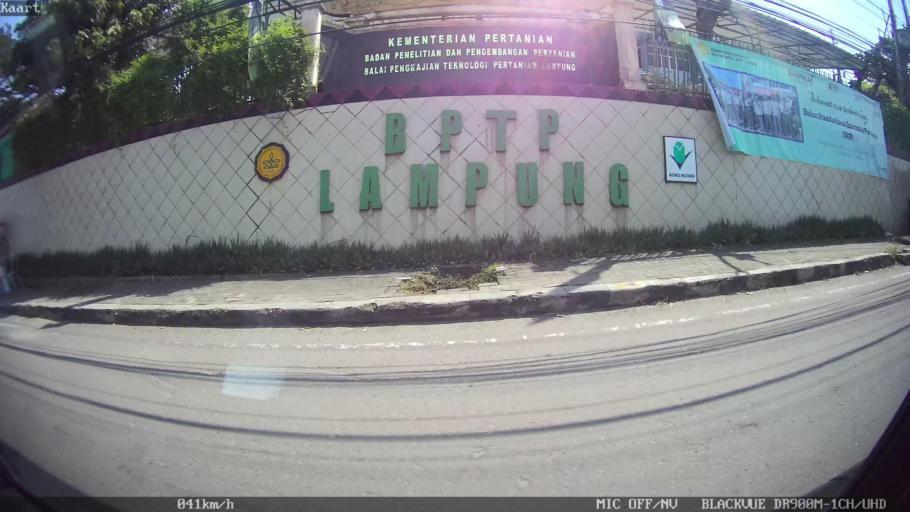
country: ID
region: Lampung
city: Kedaton
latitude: -5.3632
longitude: 105.2266
